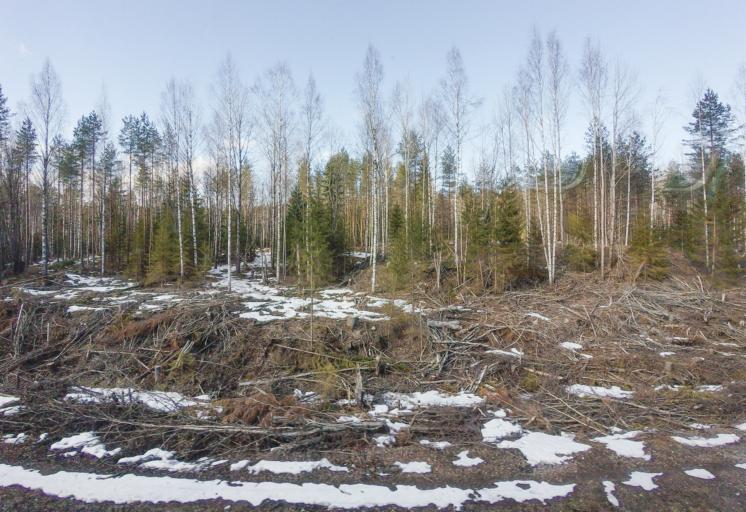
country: FI
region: South Karelia
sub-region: Lappeenranta
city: Lappeenranta
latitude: 61.0218
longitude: 28.1501
